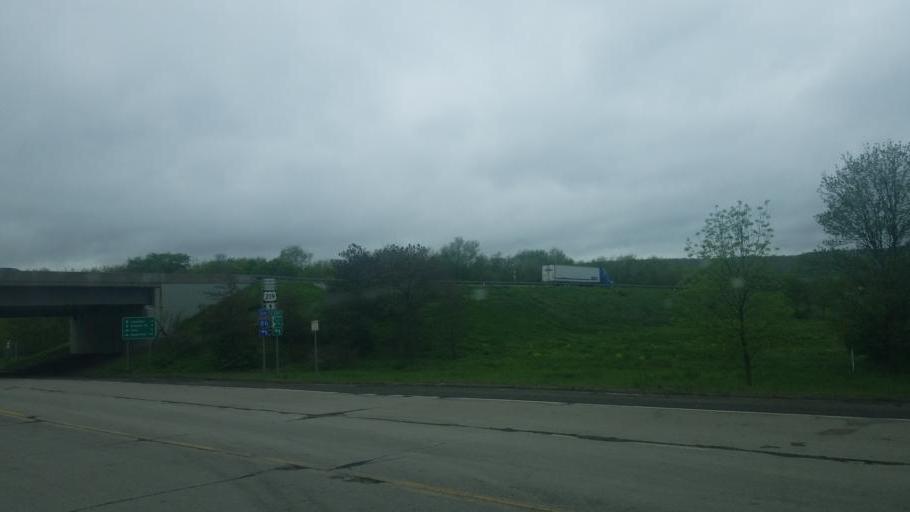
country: US
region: New York
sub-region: Cattaraugus County
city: Salamanca
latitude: 42.0888
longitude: -78.6303
